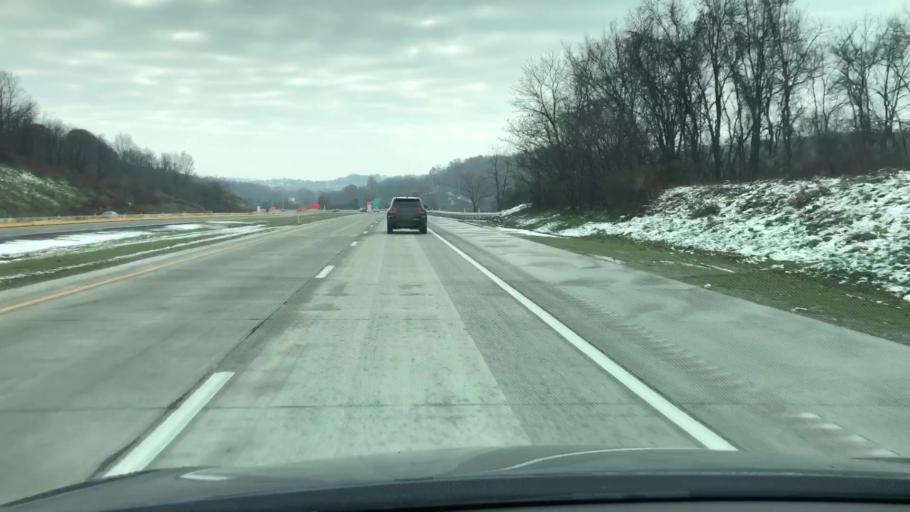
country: US
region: Pennsylvania
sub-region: Allegheny County
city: Imperial
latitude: 40.4720
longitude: -80.2483
